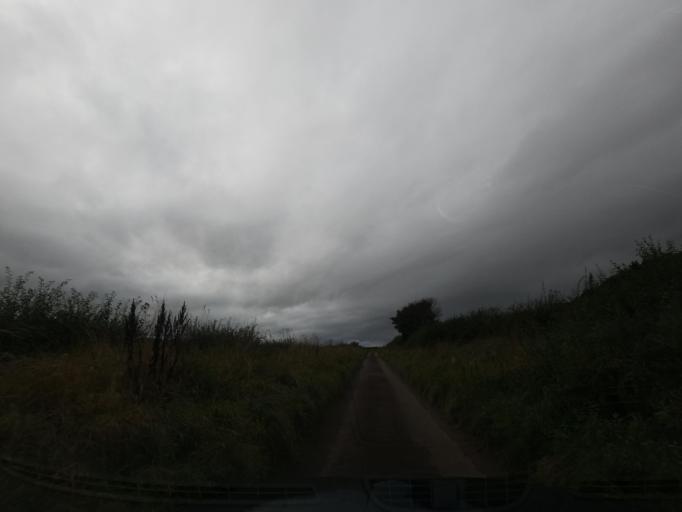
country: GB
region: England
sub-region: Northumberland
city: Ford
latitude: 55.6086
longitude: -2.0578
